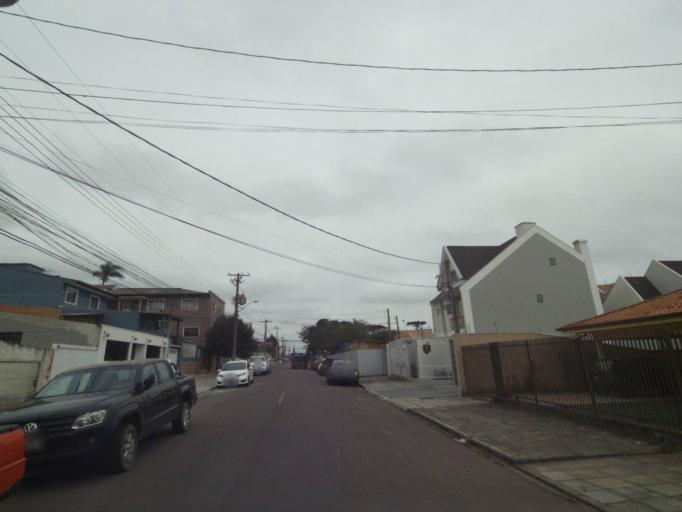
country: BR
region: Parana
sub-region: Pinhais
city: Pinhais
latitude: -25.4774
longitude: -49.2322
